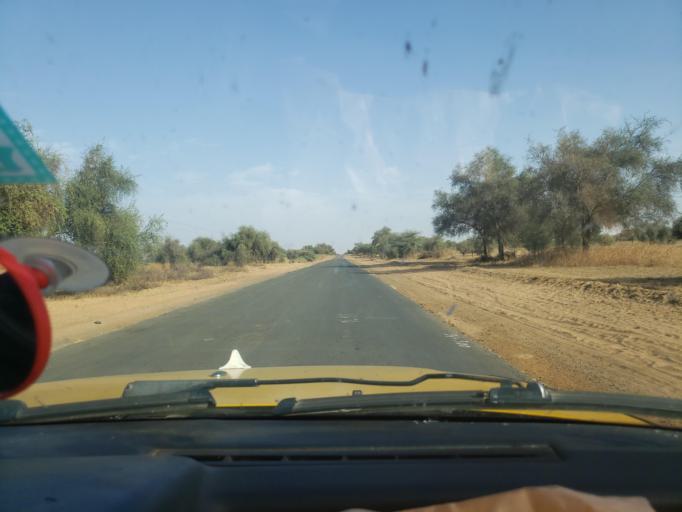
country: SN
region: Louga
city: Louga
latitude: 15.5043
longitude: -15.9540
